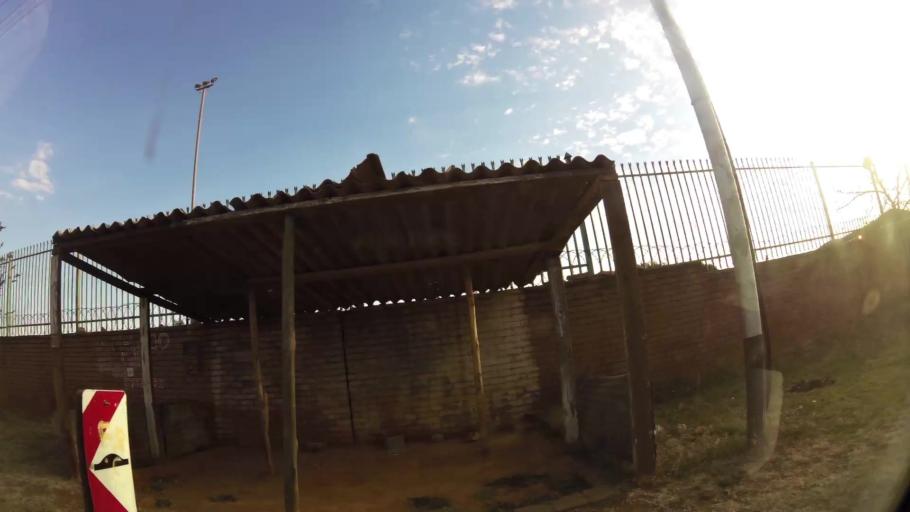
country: ZA
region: Gauteng
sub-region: City of Tshwane Metropolitan Municipality
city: Cullinan
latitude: -25.7096
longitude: 28.3789
